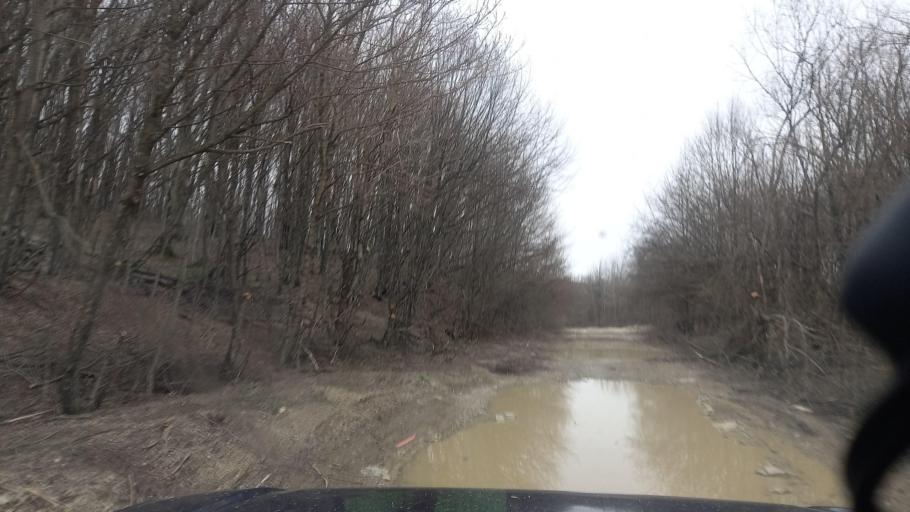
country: RU
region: Krasnodarskiy
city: Pshada
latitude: 44.5966
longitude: 38.2903
